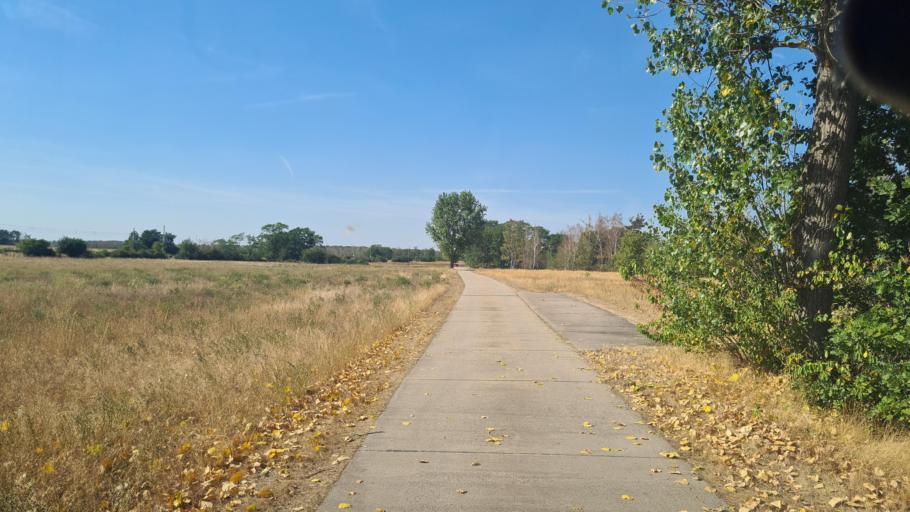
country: DE
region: Saxony
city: Zeithain
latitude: 51.3800
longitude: 13.3150
